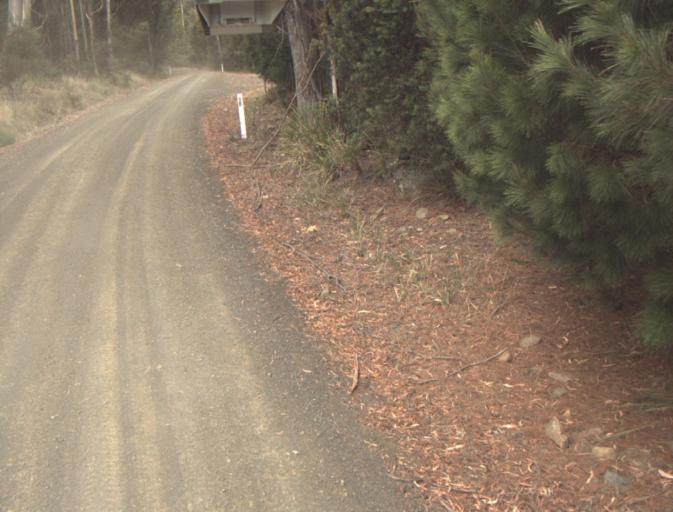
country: AU
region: Tasmania
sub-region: Launceston
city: Mayfield
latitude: -41.2745
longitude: 147.0498
